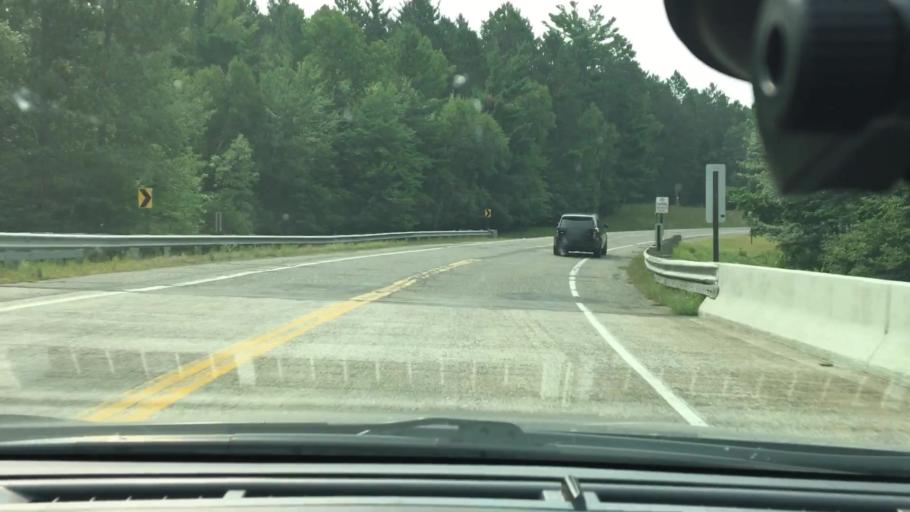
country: US
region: Minnesota
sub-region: Crow Wing County
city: Cross Lake
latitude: 46.6535
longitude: -94.0979
